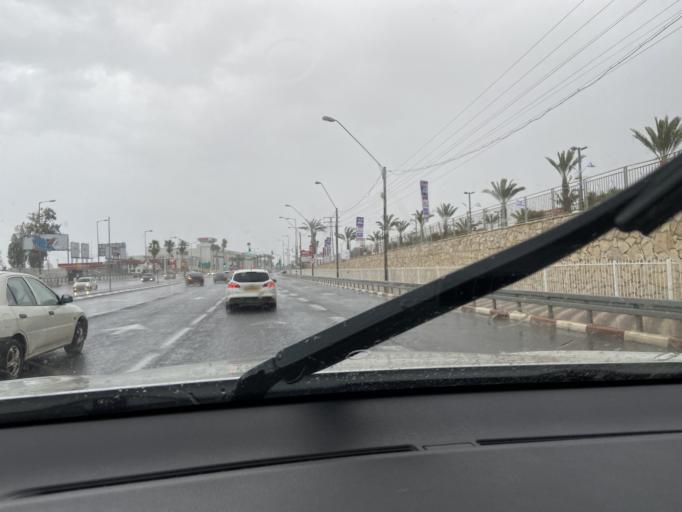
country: IL
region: Northern District
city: El Mazra`a
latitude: 32.9868
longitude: 35.0954
